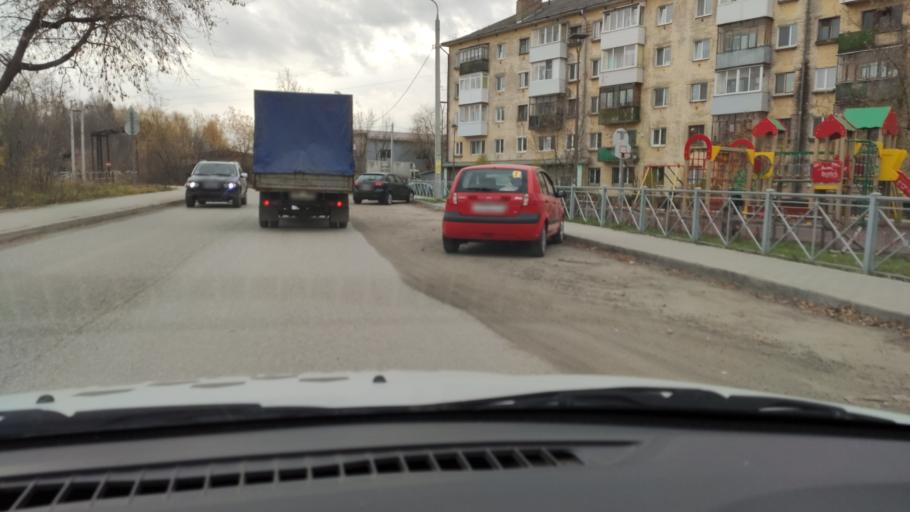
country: RU
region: Perm
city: Froly
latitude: 57.9677
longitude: 56.2735
